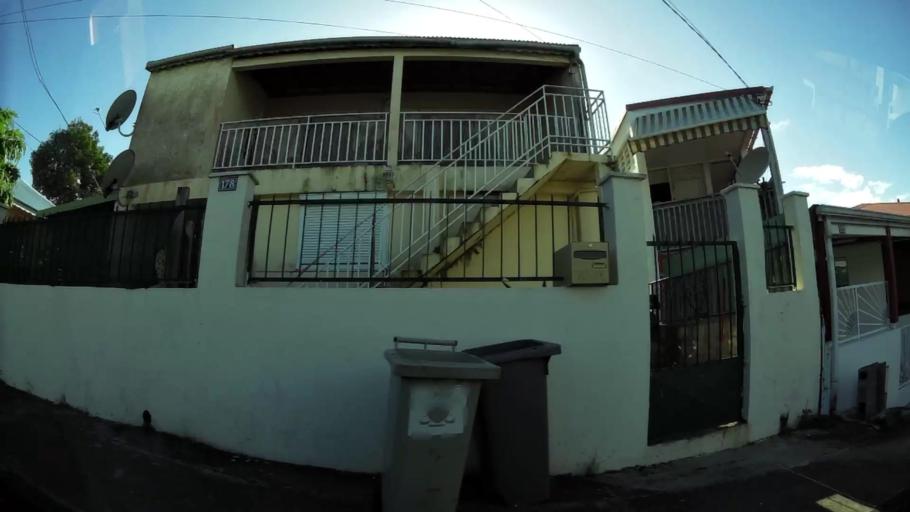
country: GP
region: Guadeloupe
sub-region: Guadeloupe
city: Le Gosier
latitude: 16.2054
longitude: -61.4812
